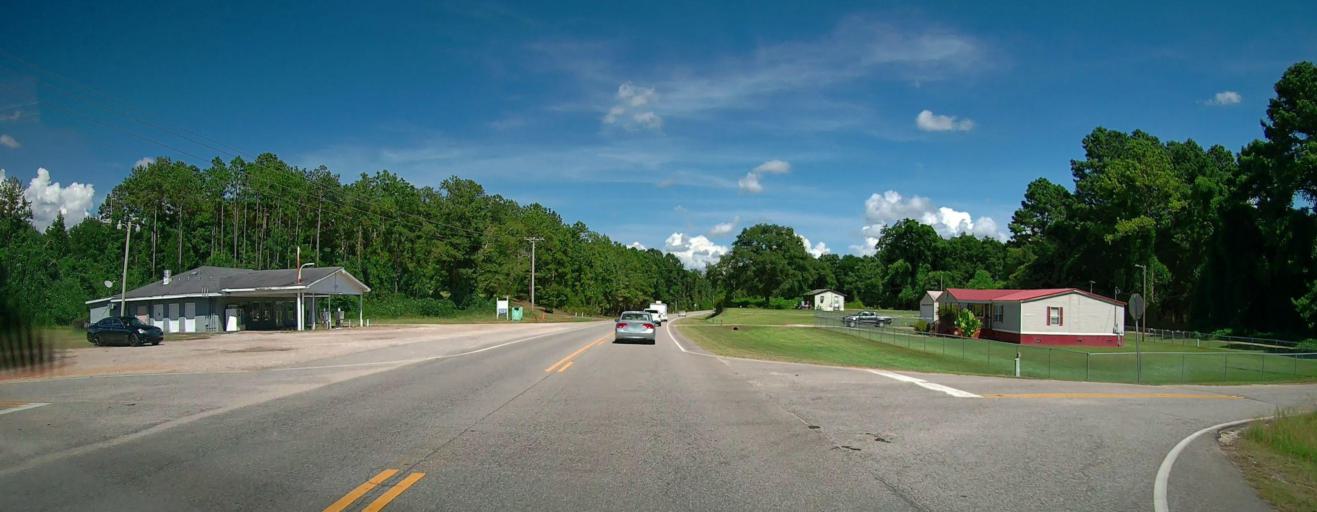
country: US
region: Alabama
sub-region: Elmore County
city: Tallassee
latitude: 32.3982
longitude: -85.9172
